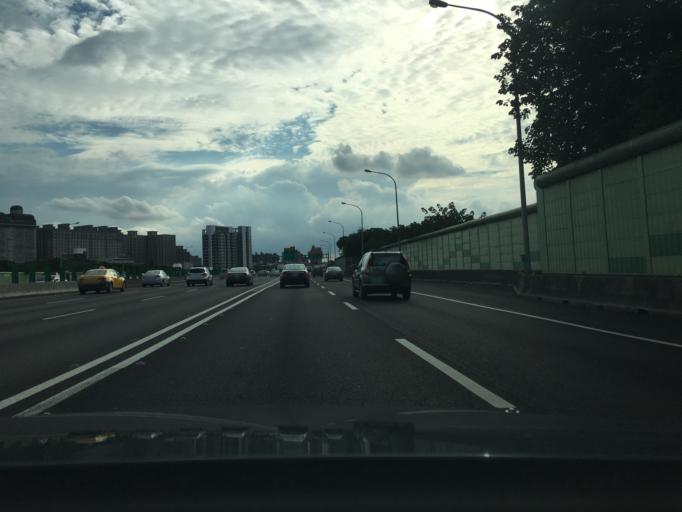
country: TW
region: Taiwan
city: Taoyuan City
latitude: 24.9696
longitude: 121.2157
